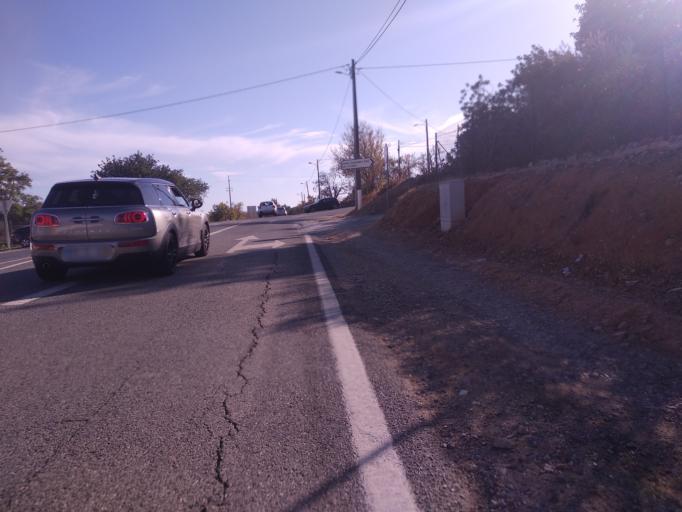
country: PT
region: Faro
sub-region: Faro
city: Santa Barbara de Nexe
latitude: 37.0953
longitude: -7.9069
